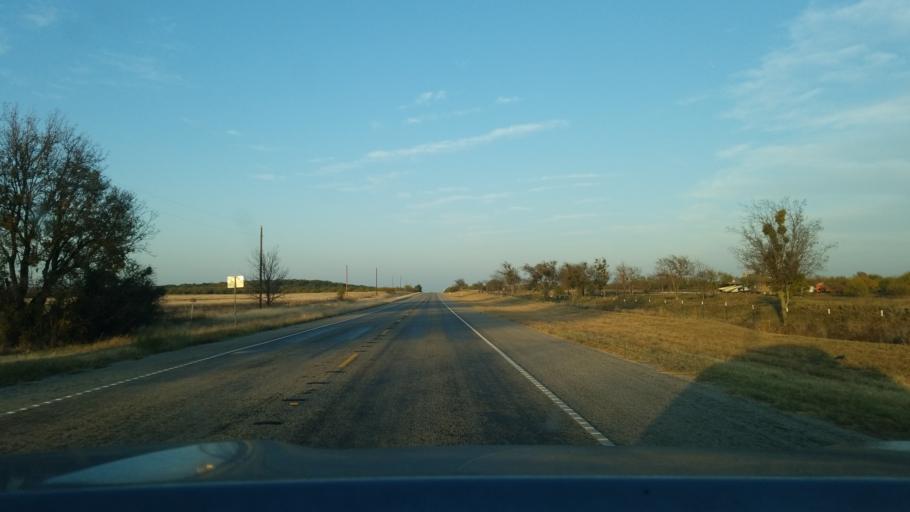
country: US
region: Texas
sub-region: Eastland County
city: Cisco
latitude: 32.4352
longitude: -98.9224
